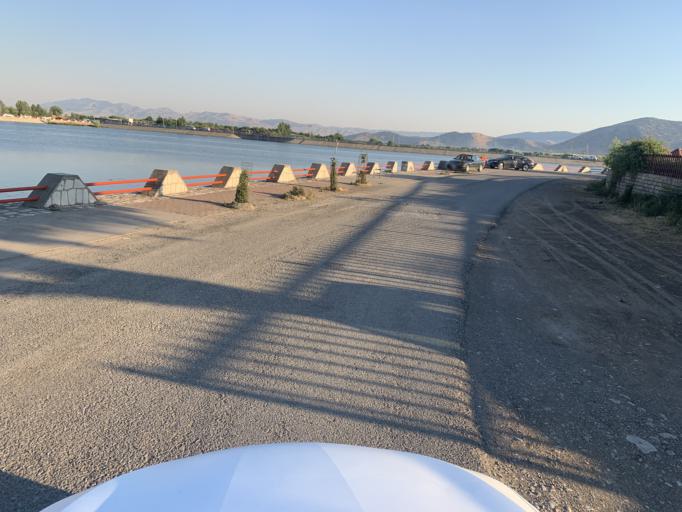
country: IQ
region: As Sulaymaniyah
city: Raniye
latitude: 36.2739
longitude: 44.7537
